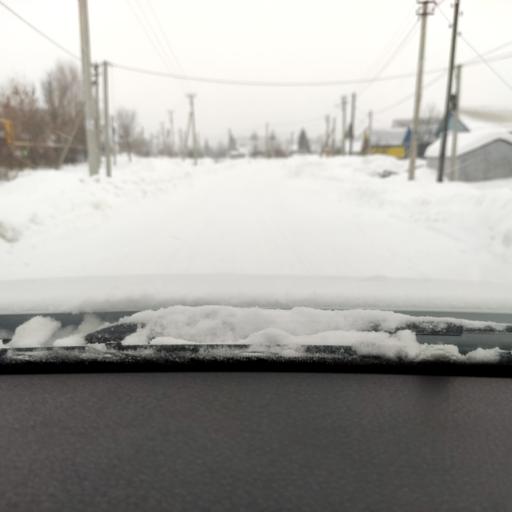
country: RU
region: Bashkortostan
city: Avdon
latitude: 54.6439
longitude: 55.7403
